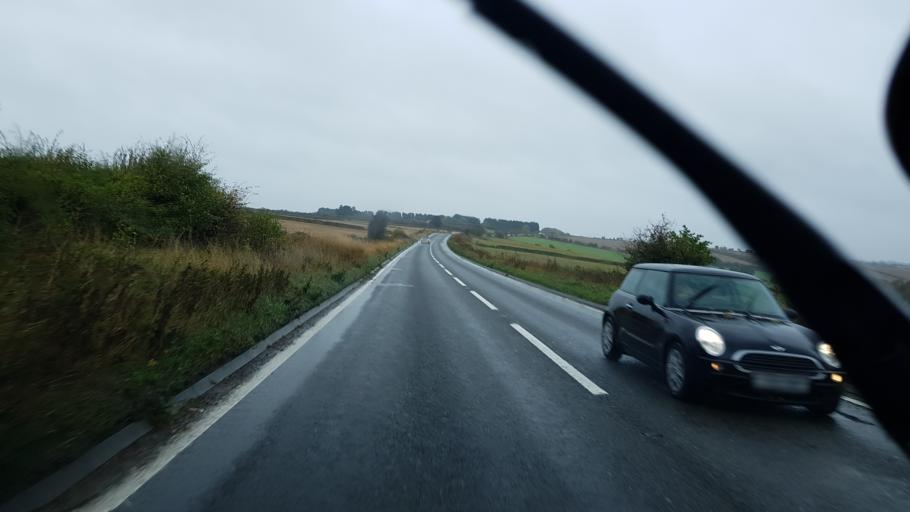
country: GB
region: England
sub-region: Oxfordshire
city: Carterton
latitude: 51.7899
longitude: -1.5866
